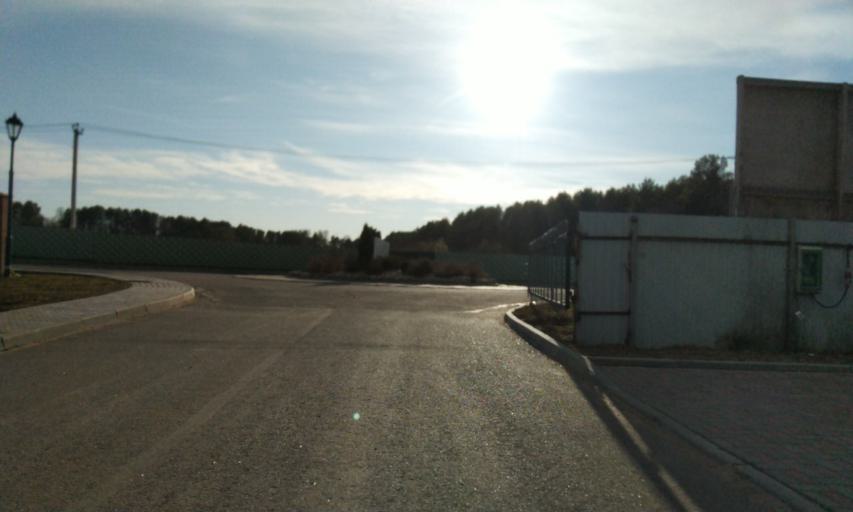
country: RU
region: Leningrad
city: Novoye Devyatkino
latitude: 60.1109
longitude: 30.4466
